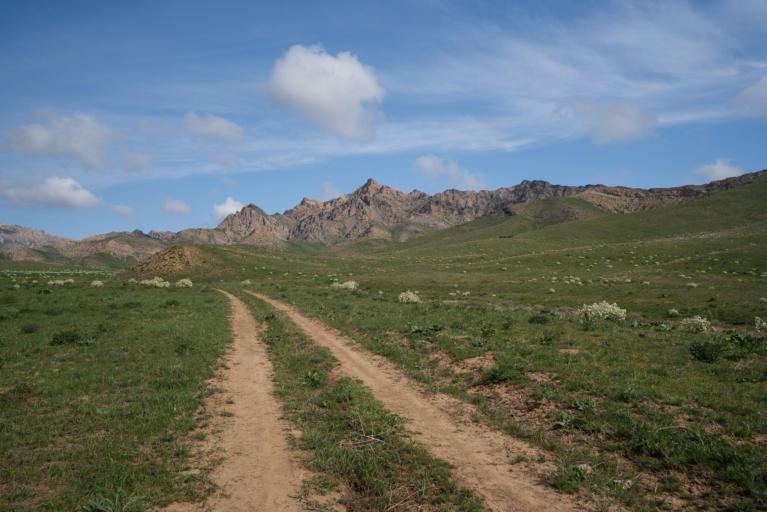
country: KZ
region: Ongtustik Qazaqstan
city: Ashchysay
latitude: 43.7210
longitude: 68.8467
